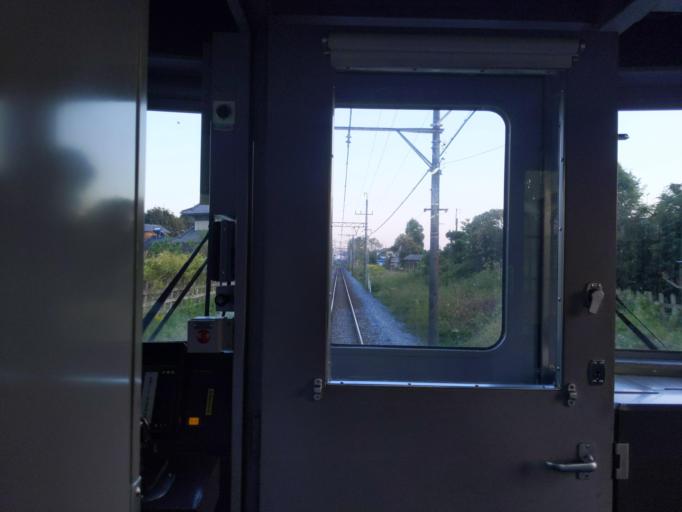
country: JP
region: Chiba
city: Noda
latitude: 35.9681
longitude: 139.8546
